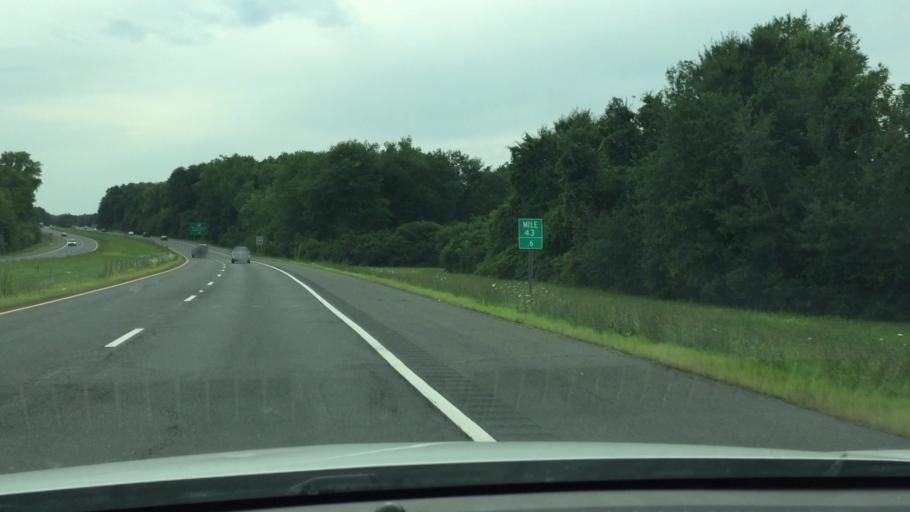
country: US
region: Massachusetts
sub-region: Hampden County
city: Agawam
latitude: 42.0759
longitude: -72.6202
